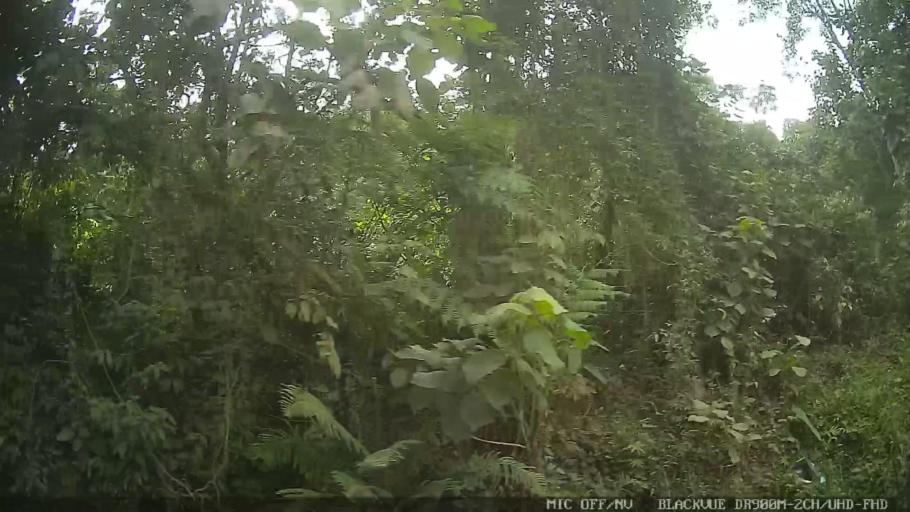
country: BR
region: Sao Paulo
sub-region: Mogi das Cruzes
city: Mogi das Cruzes
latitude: -23.5214
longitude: -46.2309
